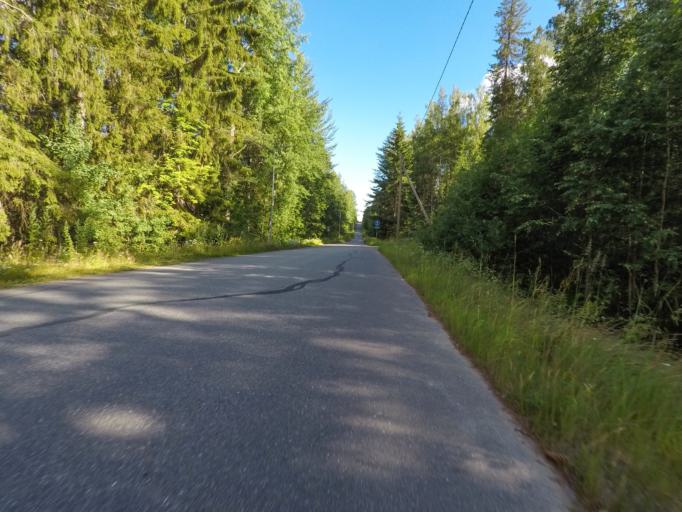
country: FI
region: South Karelia
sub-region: Lappeenranta
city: Lappeenranta
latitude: 61.0942
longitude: 28.1383
